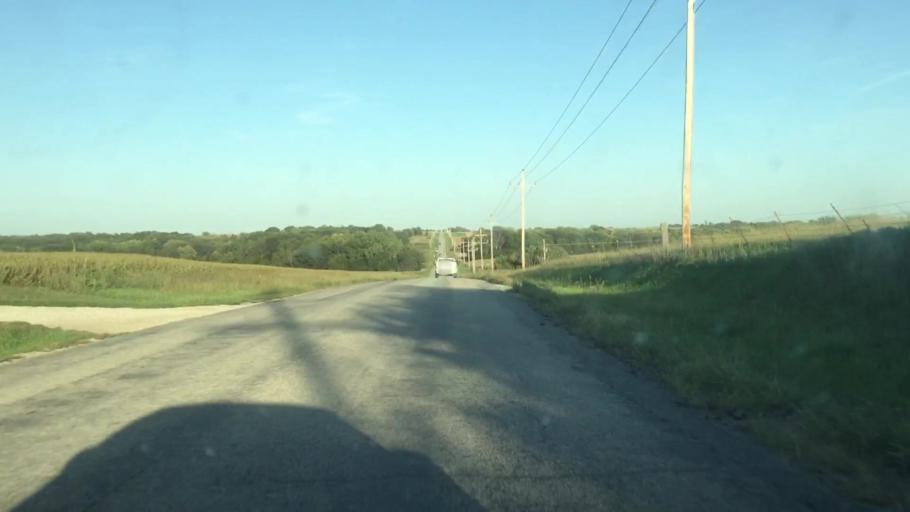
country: US
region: Kansas
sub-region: Brown County
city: Horton
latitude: 39.5656
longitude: -95.3865
